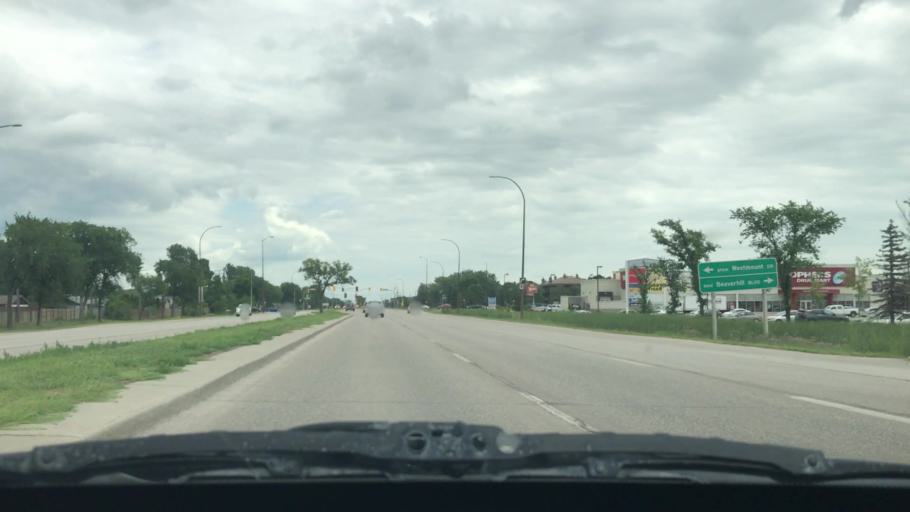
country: CA
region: Manitoba
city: Winnipeg
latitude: 49.8560
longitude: -97.0689
